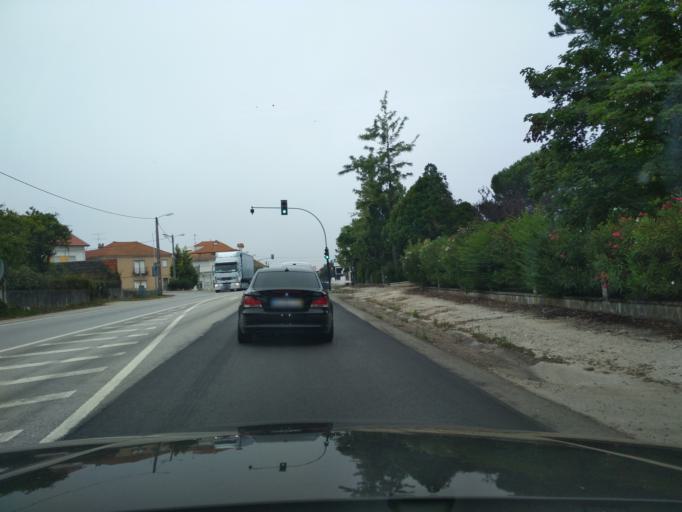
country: PT
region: Aveiro
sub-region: Mealhada
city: Pampilhosa do Botao
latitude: 40.3045
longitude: -8.4481
